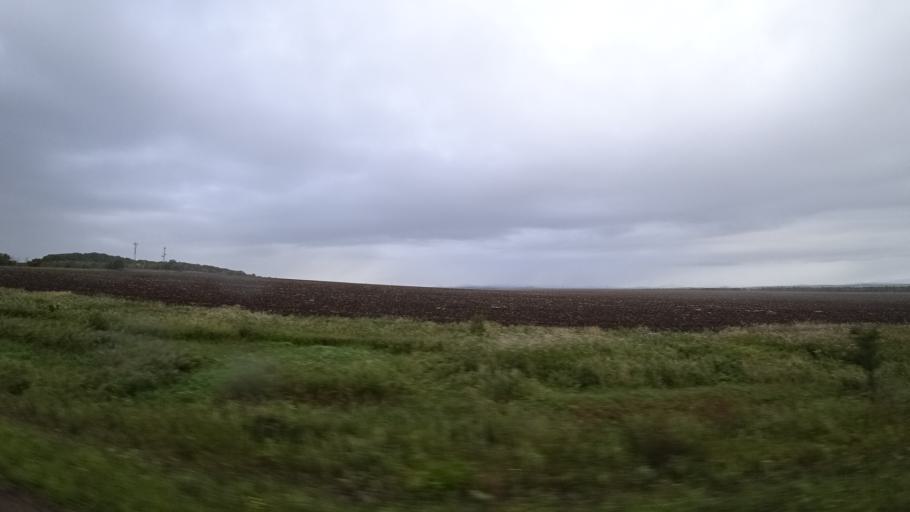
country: RU
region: Primorskiy
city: Chernigovka
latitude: 44.3651
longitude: 132.5401
